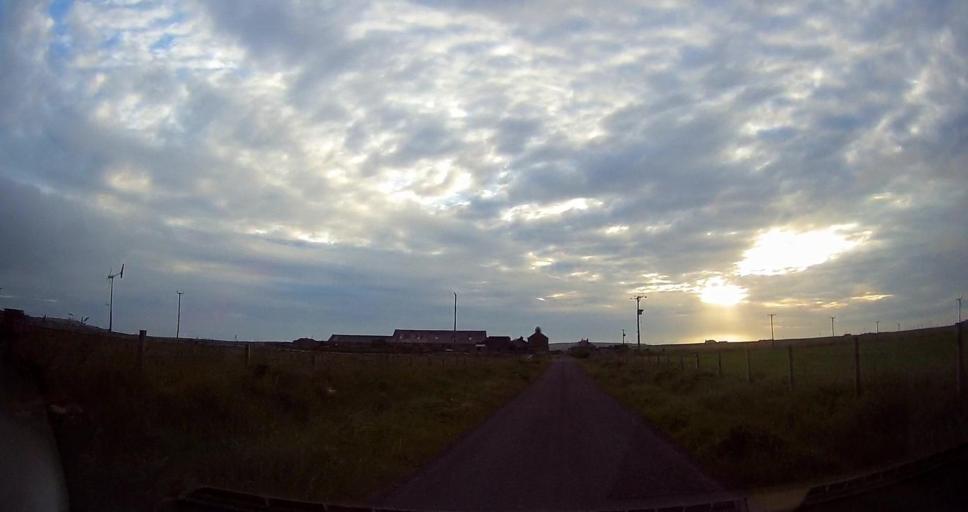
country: GB
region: Scotland
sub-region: Orkney Islands
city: Stromness
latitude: 59.1265
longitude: -3.2900
